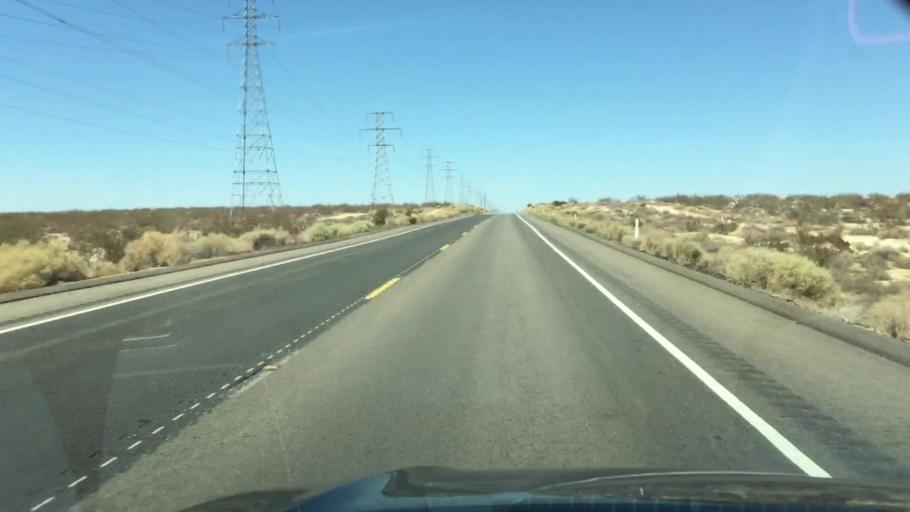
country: US
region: California
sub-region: Kern County
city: Boron
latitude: 35.0900
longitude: -117.5687
